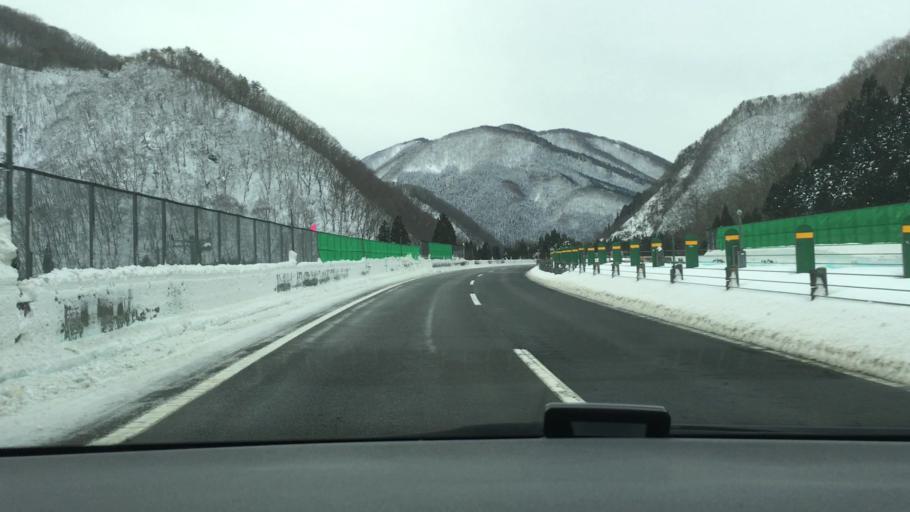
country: JP
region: Akita
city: Hanawa
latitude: 40.1219
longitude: 140.9056
